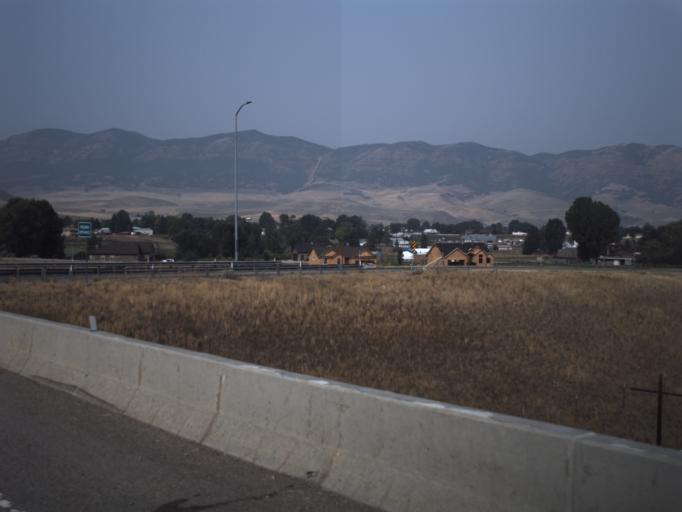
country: US
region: Utah
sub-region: Summit County
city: Coalville
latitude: 41.0164
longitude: -111.4888
